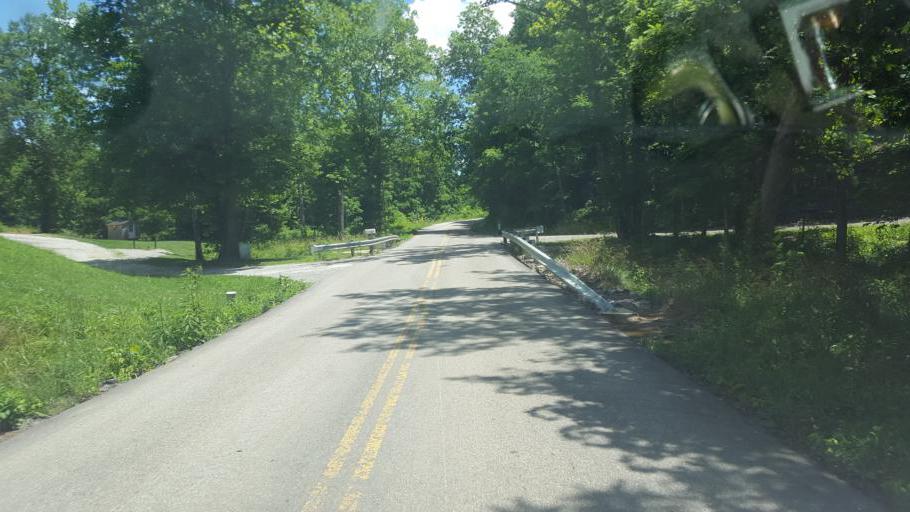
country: US
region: Ohio
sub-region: Gallia County
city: Gallipolis
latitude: 38.7214
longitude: -82.3553
